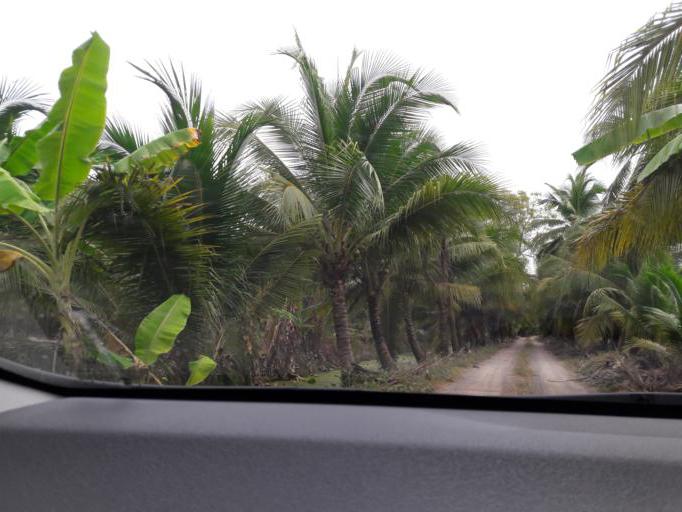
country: TH
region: Ratchaburi
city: Damnoen Saduak
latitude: 13.5691
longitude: 100.0236
